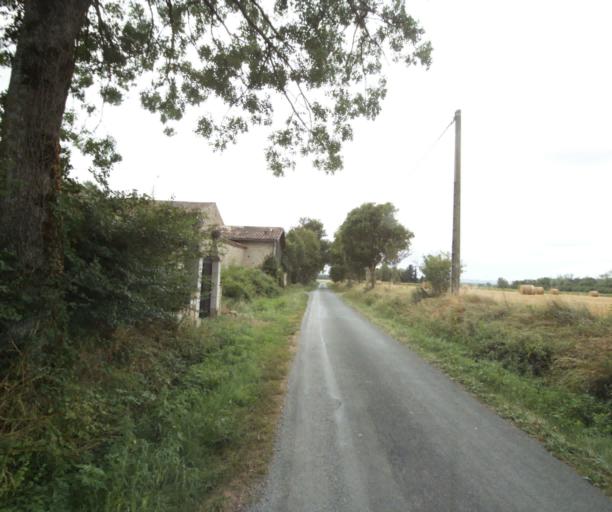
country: FR
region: Midi-Pyrenees
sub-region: Departement du Tarn
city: Soreze
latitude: 43.4599
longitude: 2.0560
